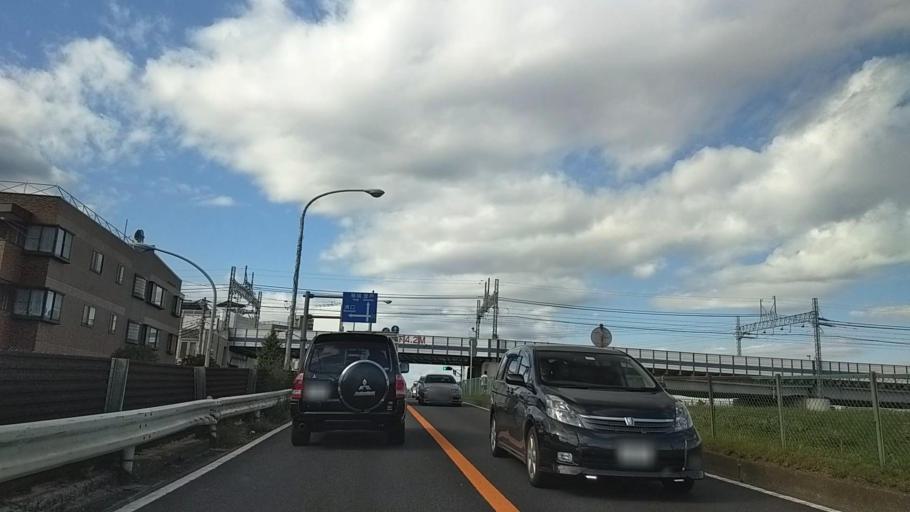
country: JP
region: Tokyo
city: Chofugaoka
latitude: 35.6074
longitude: 139.6242
